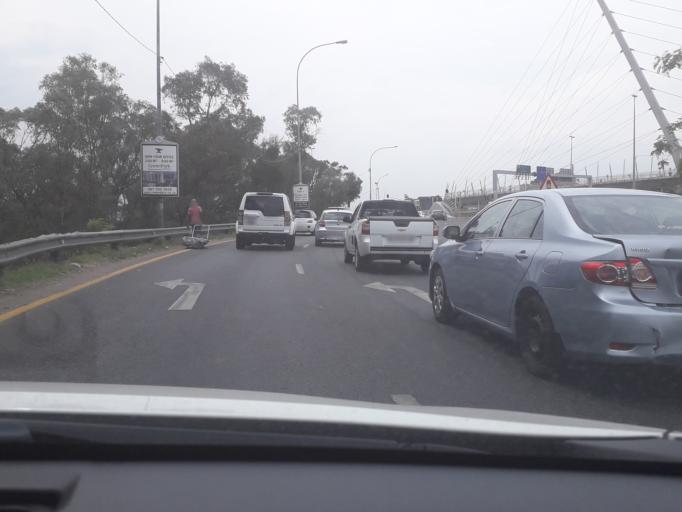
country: ZA
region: Gauteng
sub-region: City of Johannesburg Metropolitan Municipality
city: Modderfontein
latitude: -26.1089
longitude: 28.0755
